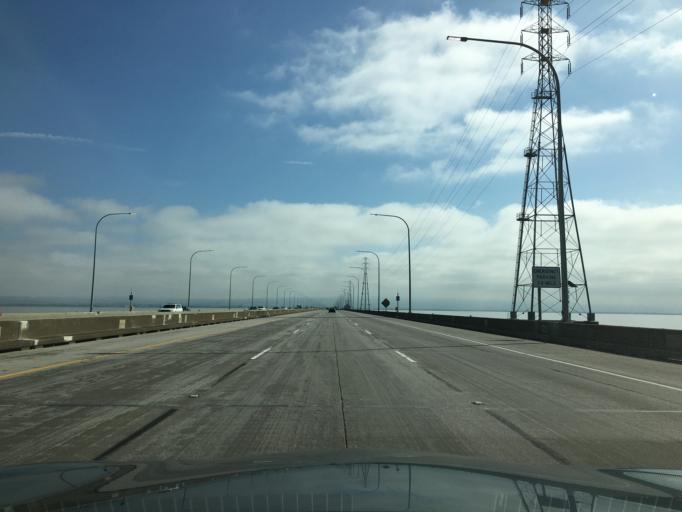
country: US
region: California
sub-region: San Mateo County
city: Foster City
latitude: 37.6014
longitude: -122.2072
